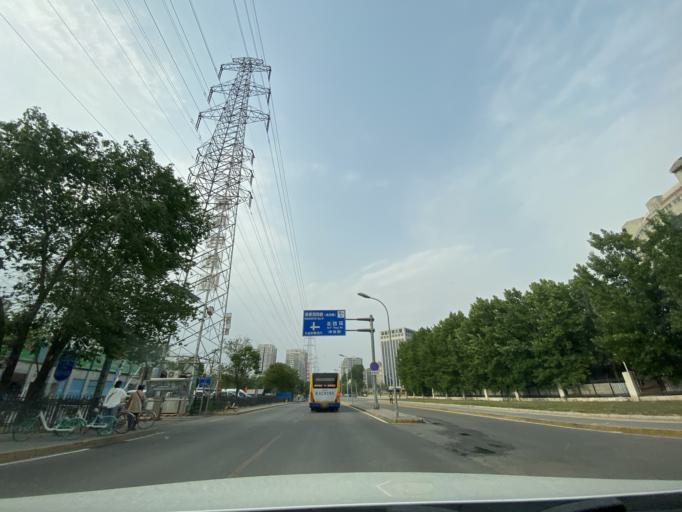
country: CN
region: Beijing
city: Qinghe
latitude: 39.9839
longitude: 116.3345
